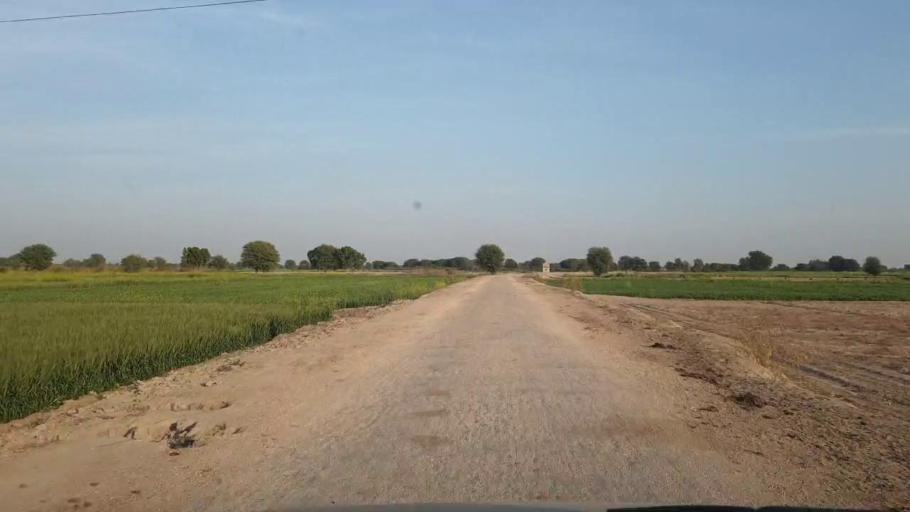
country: PK
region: Sindh
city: Chambar
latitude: 25.2605
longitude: 68.7995
